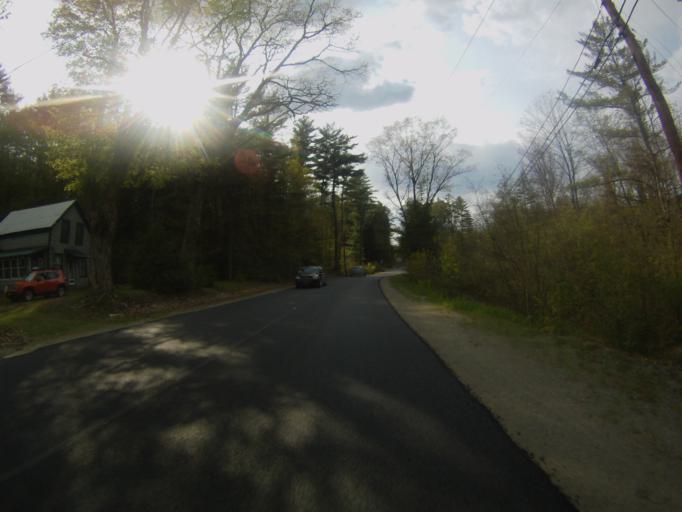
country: US
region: New York
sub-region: Warren County
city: Warrensburg
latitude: 43.8361
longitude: -73.7755
